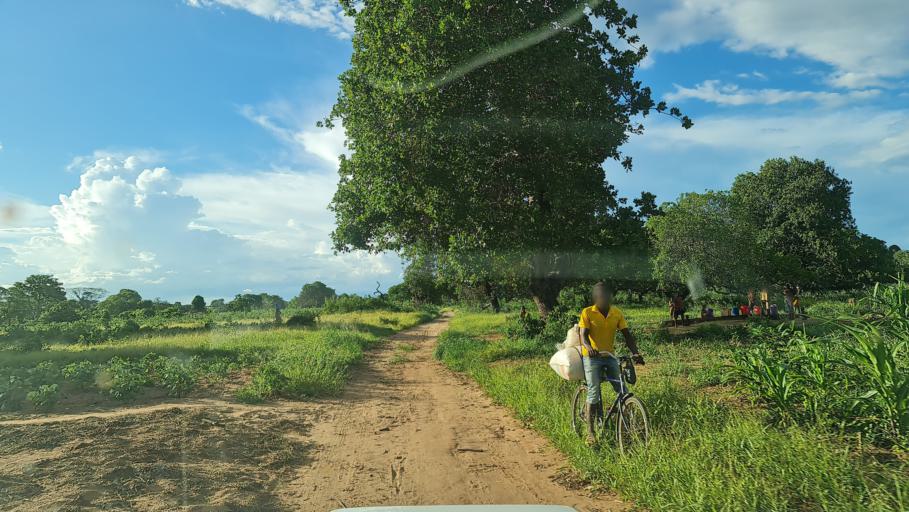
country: MZ
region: Nampula
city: Ilha de Mocambique
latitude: -14.9483
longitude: 40.1689
